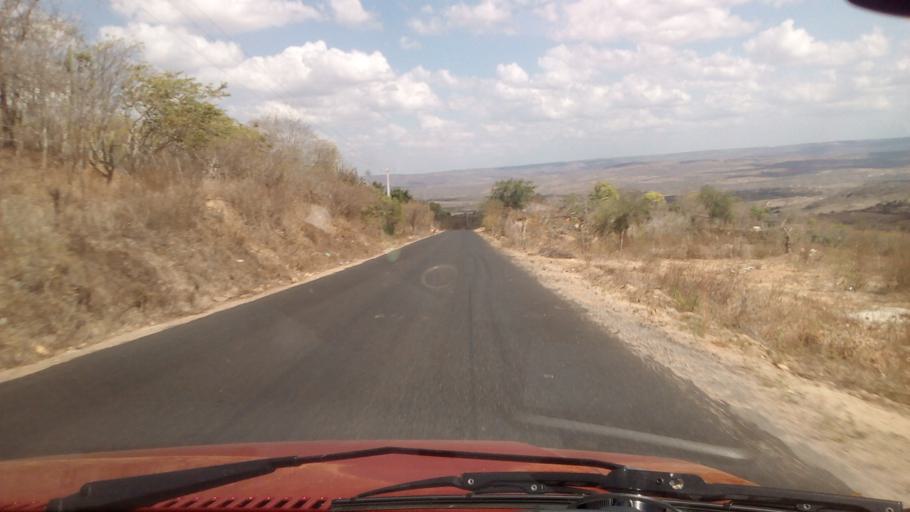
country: BR
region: Paraiba
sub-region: Cacimba De Dentro
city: Cacimba de Dentro
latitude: -6.6503
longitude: -35.7784
